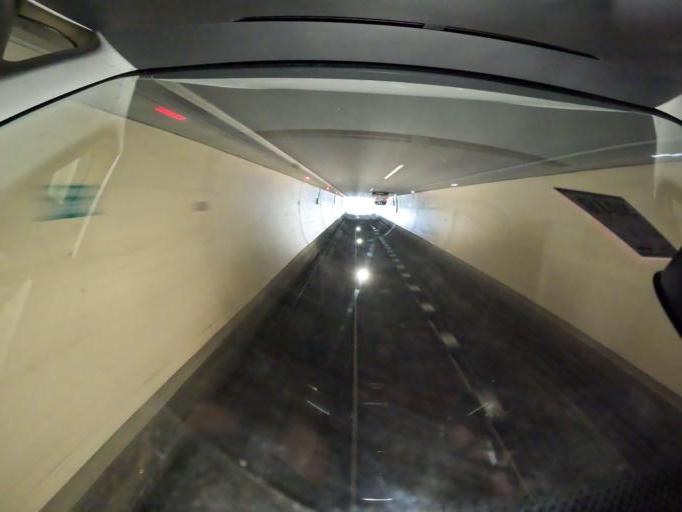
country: AT
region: Carinthia
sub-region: Politischer Bezirk Wolfsberg
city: Bad Sankt Leonhard im Lavanttal
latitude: 46.9187
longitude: 14.8248
